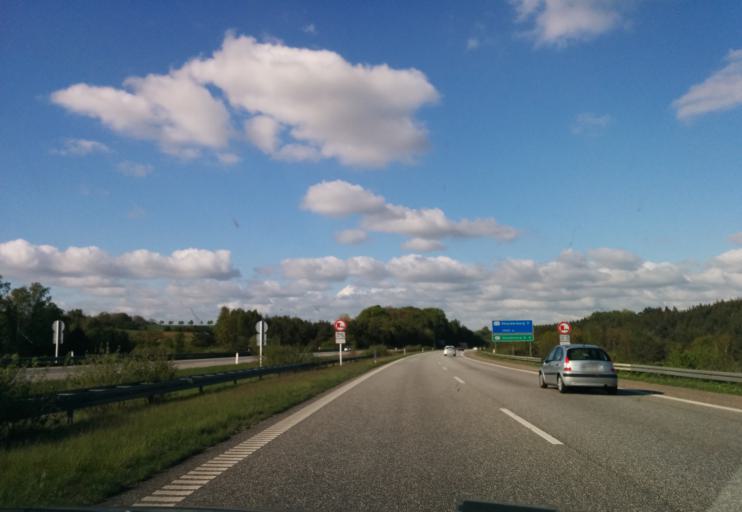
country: DK
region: Central Jutland
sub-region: Skanderborg Kommune
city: Skanderborg
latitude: 56.0341
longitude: 9.8841
